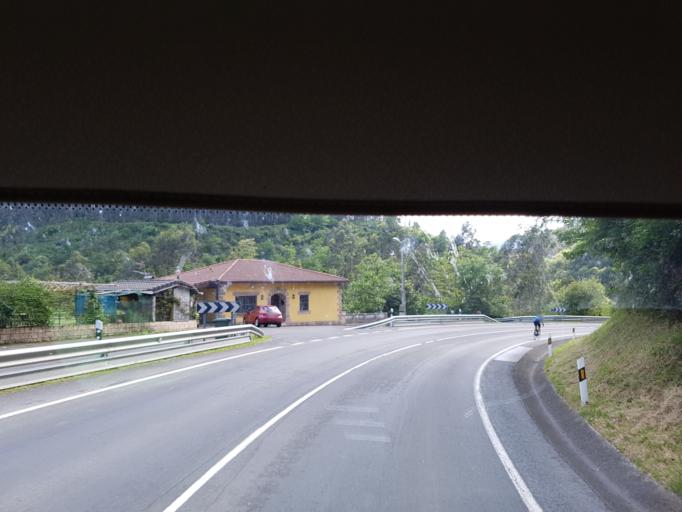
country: ES
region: Basque Country
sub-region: Bizkaia
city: Sopuerta
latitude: 43.2893
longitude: -3.1310
